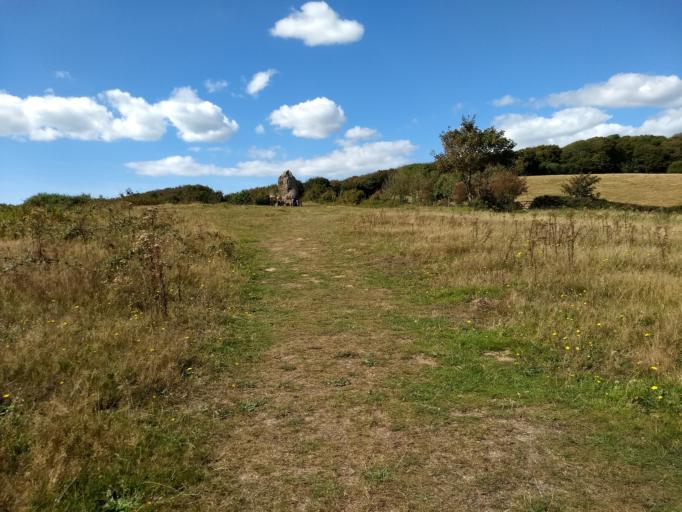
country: GB
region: England
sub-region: Isle of Wight
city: Shalfleet
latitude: 50.6561
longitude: -1.4246
